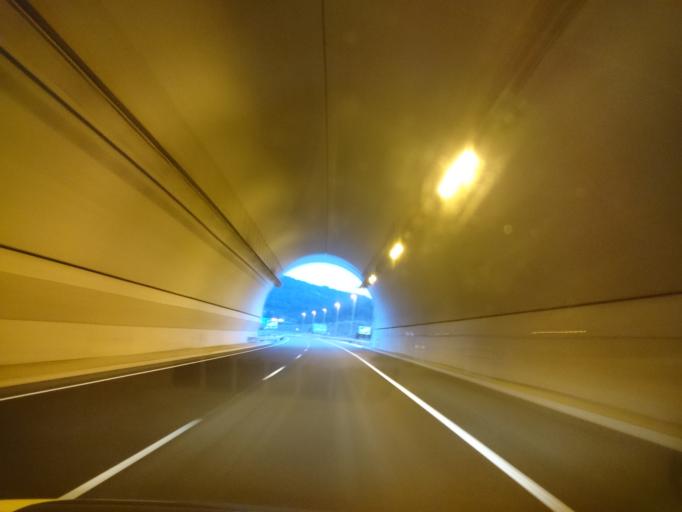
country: ES
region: Catalonia
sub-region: Provincia de Barcelona
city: Sant Pere de Ribes
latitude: 41.2796
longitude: 1.7293
